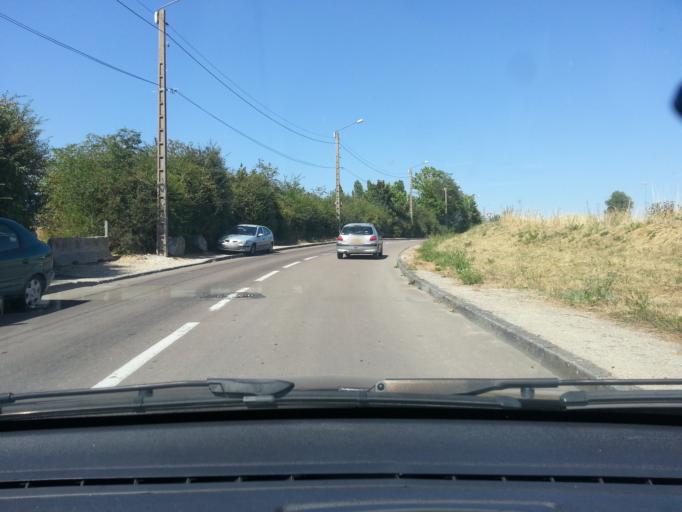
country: FR
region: Bourgogne
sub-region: Departement de la Cote-d'Or
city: Longvic
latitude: 47.3035
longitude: 5.0711
